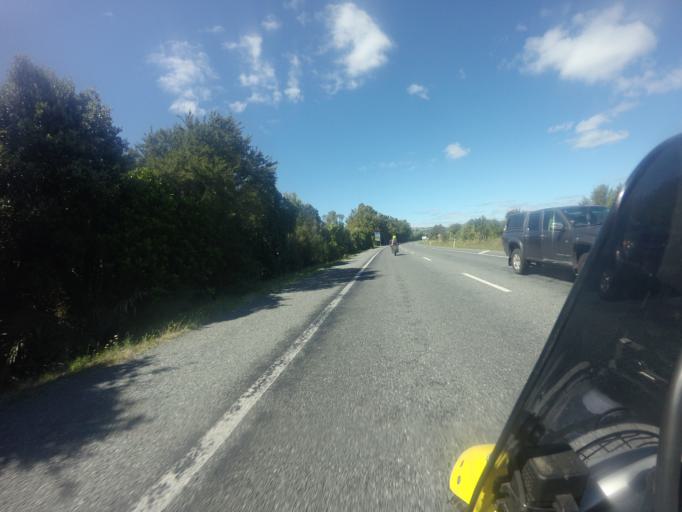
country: NZ
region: Bay of Plenty
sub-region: Whakatane District
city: Whakatane
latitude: -37.9513
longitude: 176.9584
